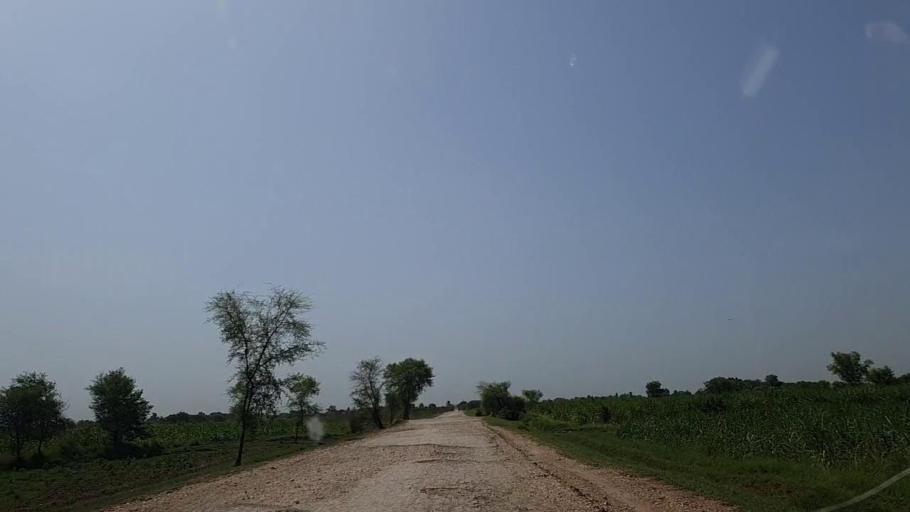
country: PK
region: Sindh
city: Naushahro Firoz
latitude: 26.8549
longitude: 68.0079
